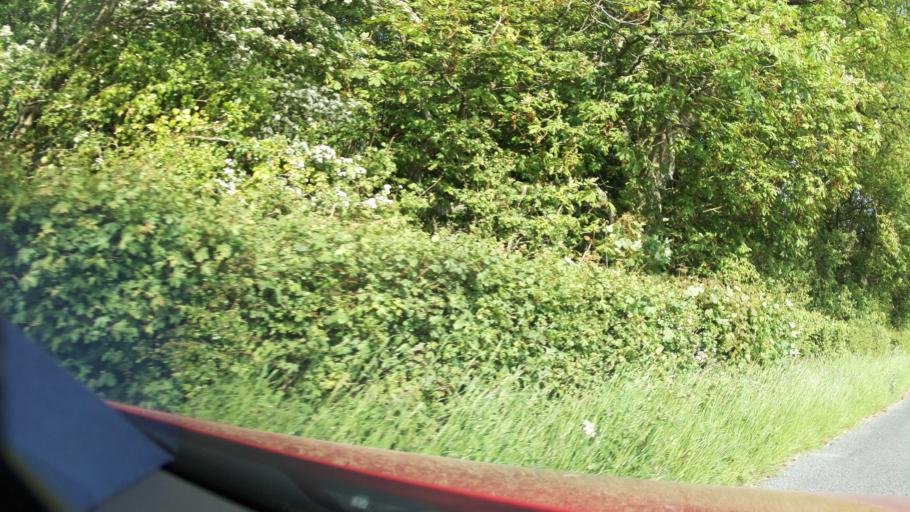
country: GB
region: England
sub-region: Gloucestershire
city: Chipping Campden
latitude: 52.0570
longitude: -1.8065
